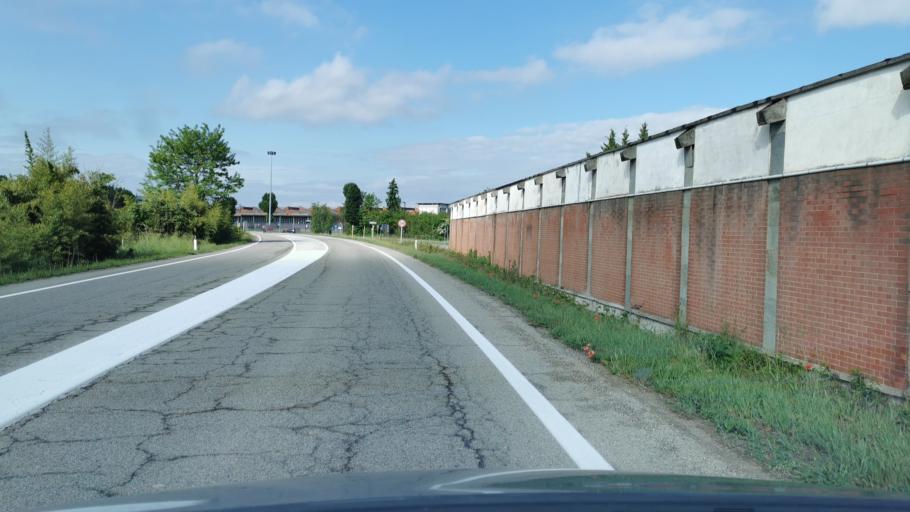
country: IT
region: Piedmont
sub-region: Provincia di Torino
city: Santena
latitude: 44.9370
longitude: 7.7626
